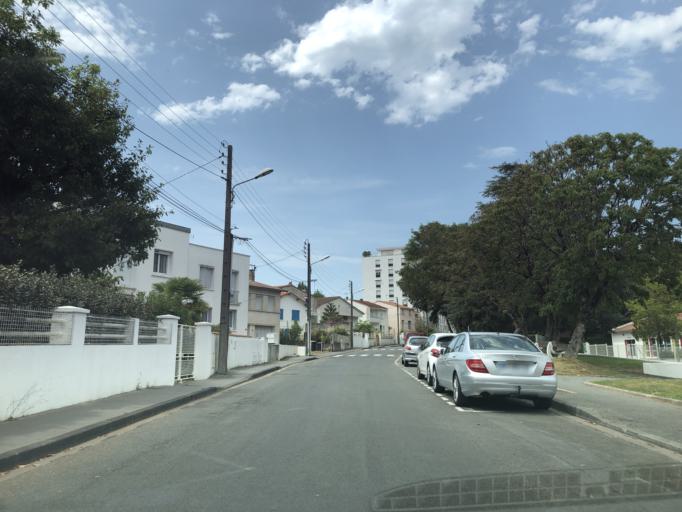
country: FR
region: Poitou-Charentes
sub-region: Departement de la Charente-Maritime
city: Royan
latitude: 45.6239
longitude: -1.0341
